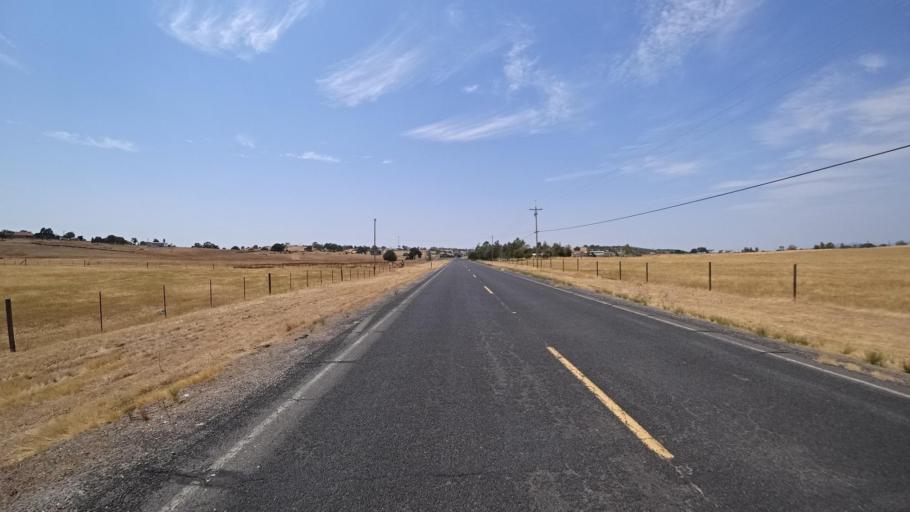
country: US
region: California
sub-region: Tuolumne County
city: Jamestown
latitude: 37.6455
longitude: -120.3210
